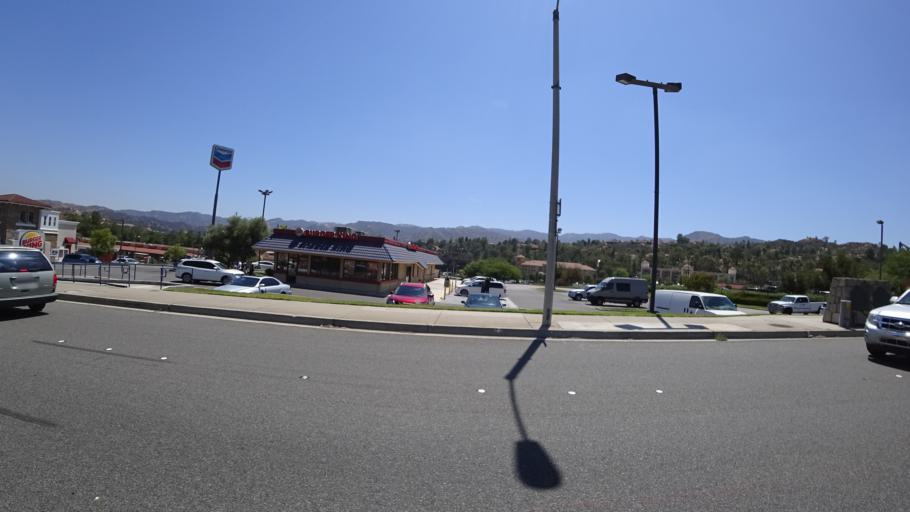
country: US
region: California
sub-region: Los Angeles County
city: Santa Clarita
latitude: 34.3784
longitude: -118.5638
